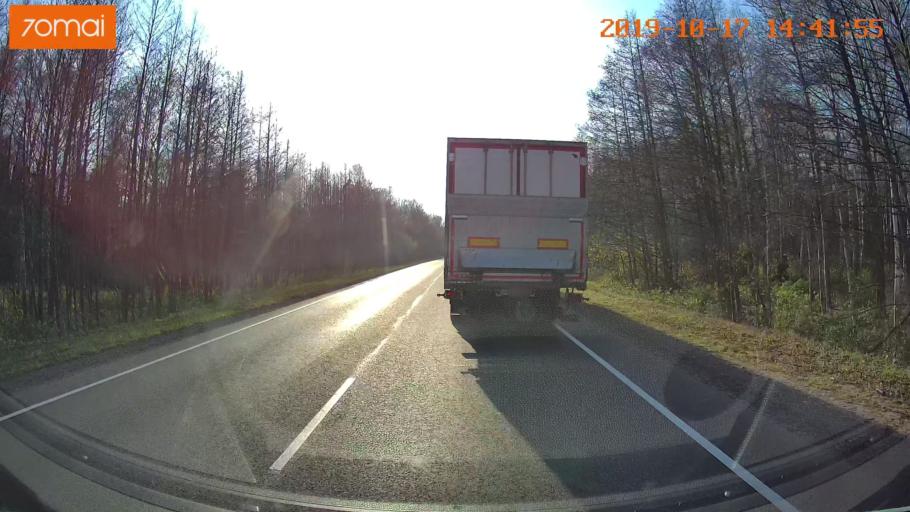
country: RU
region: Rjazan
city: Solotcha
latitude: 54.8416
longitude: 39.9335
